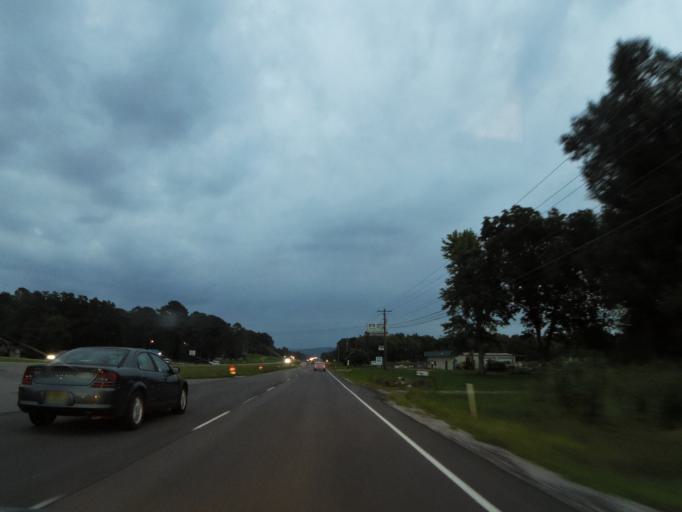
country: US
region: Alabama
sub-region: Madison County
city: Moores Mill
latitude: 34.7515
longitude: -86.4613
